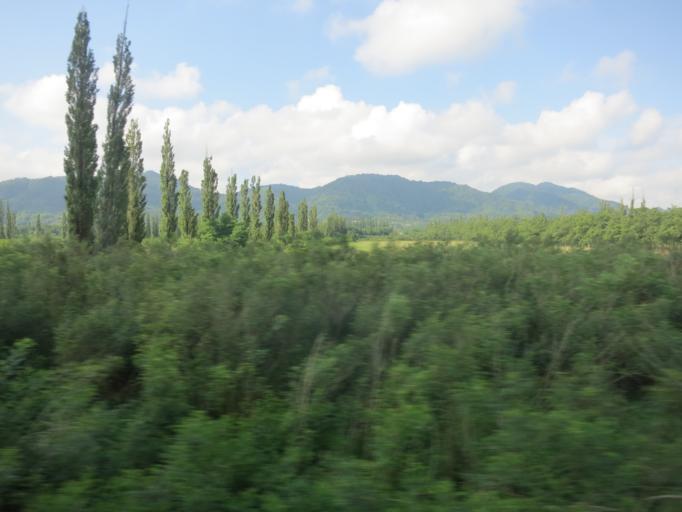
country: GE
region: Guria
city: Lanchkhuti
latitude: 42.0873
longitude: 42.0614
